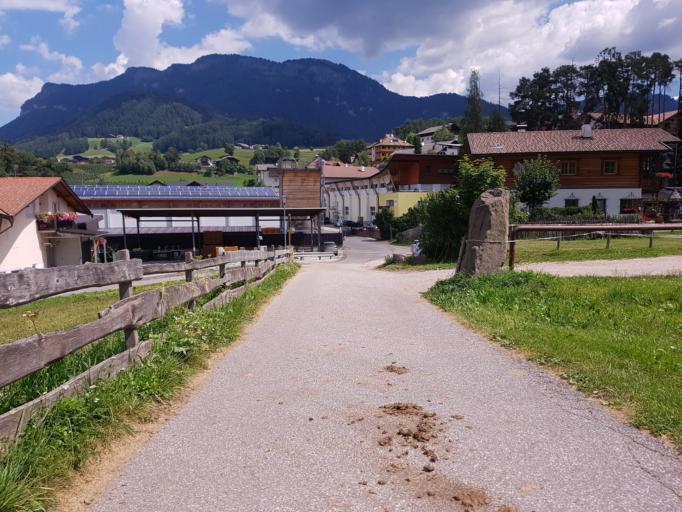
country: IT
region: Trentino-Alto Adige
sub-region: Bolzano
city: Castelrotto
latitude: 46.5573
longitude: 11.5511
